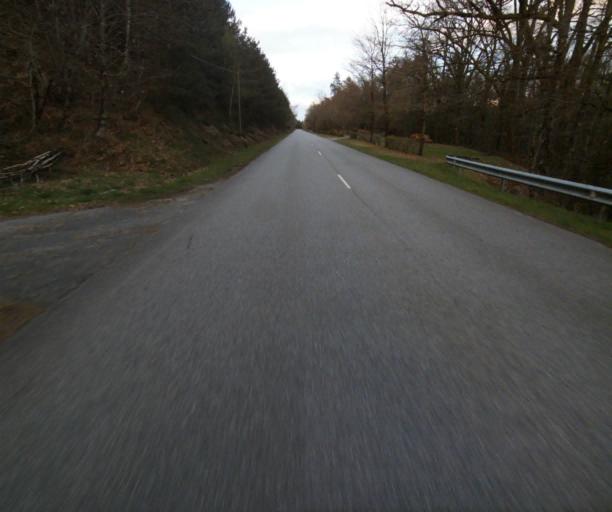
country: FR
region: Limousin
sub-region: Departement de la Correze
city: Correze
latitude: 45.2895
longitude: 1.8780
